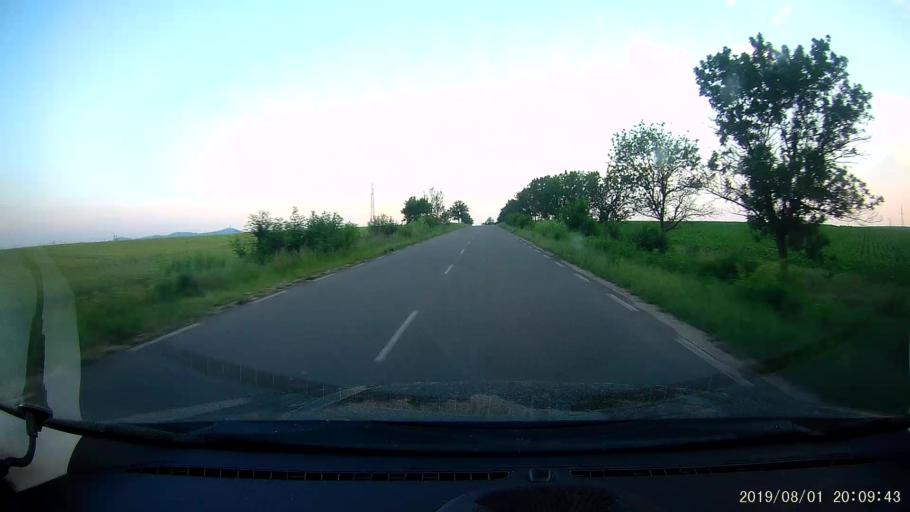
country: BG
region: Yambol
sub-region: Obshtina Yambol
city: Yambol
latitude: 42.4940
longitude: 26.5938
